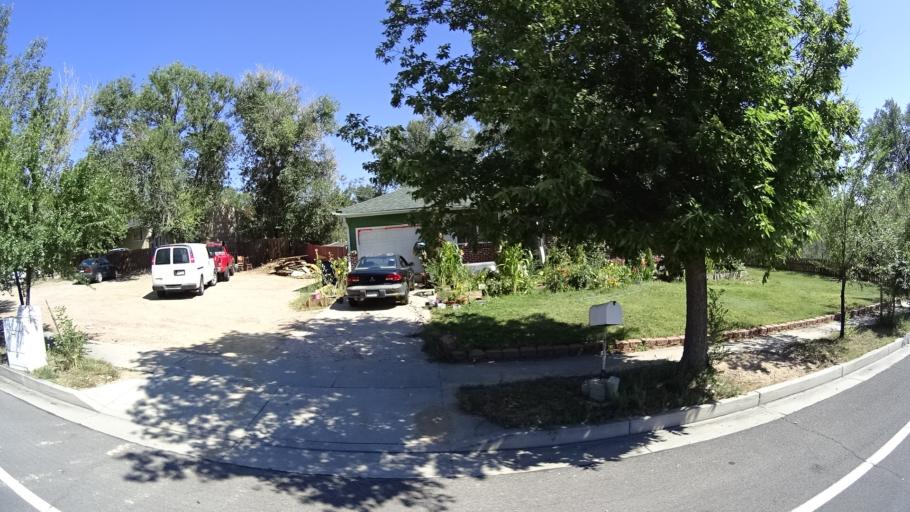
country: US
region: Colorado
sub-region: El Paso County
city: Cimarron Hills
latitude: 38.8309
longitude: -104.7486
